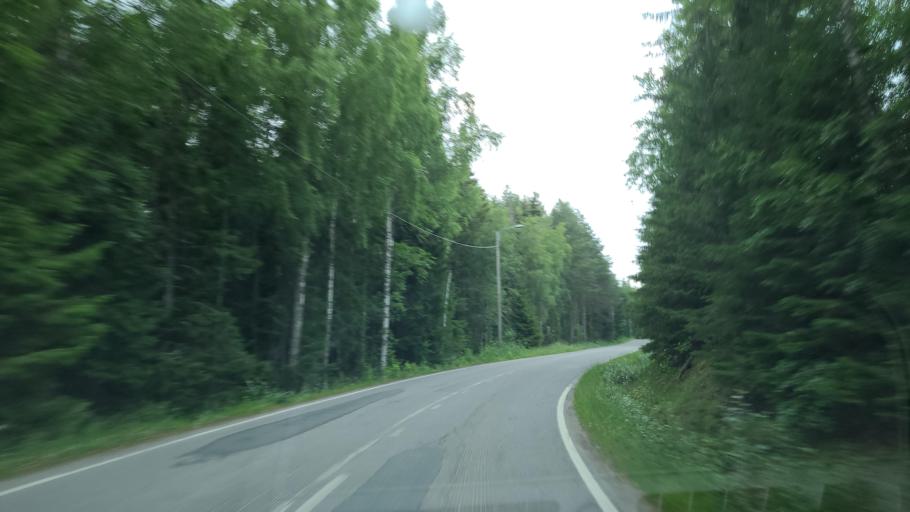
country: FI
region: Ostrobothnia
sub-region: Vaasa
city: Replot
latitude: 63.1757
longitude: 21.2761
